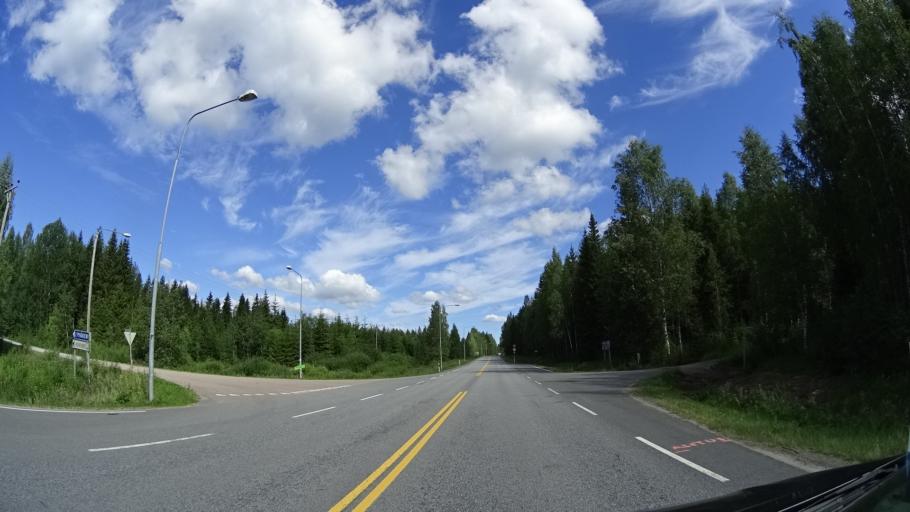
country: FI
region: Pirkanmaa
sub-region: Luoteis-Pirkanmaa
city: Kihnioe
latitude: 62.1899
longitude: 23.1717
